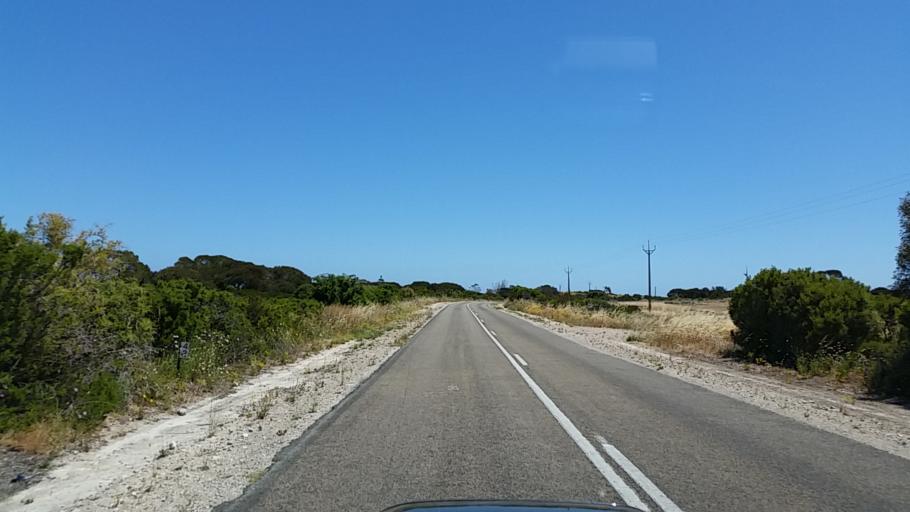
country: AU
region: South Australia
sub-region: Yorke Peninsula
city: Honiton
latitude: -35.2225
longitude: 136.9943
